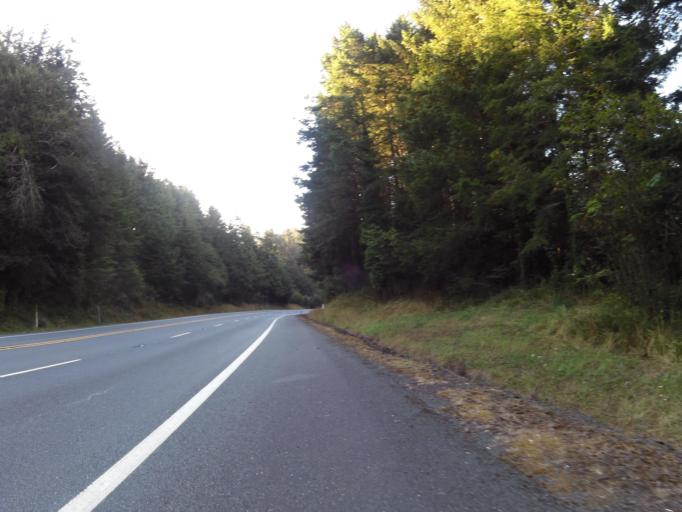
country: US
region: Oregon
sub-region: Curry County
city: Gold Beach
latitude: 42.3566
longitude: -124.4130
